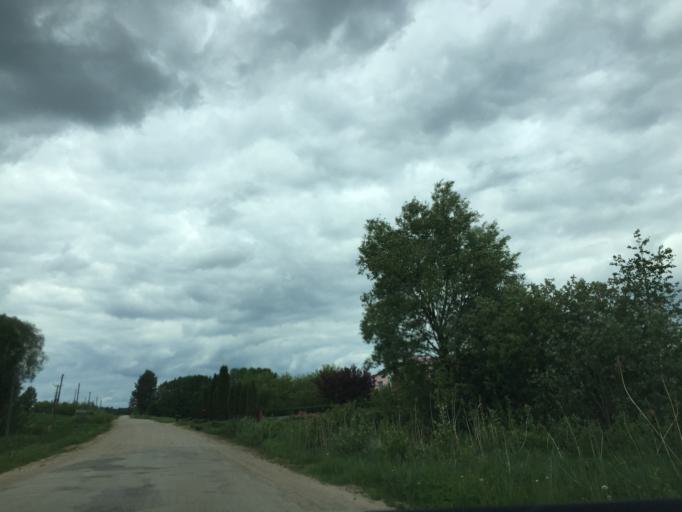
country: LV
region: Dagda
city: Dagda
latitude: 55.9773
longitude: 27.6055
